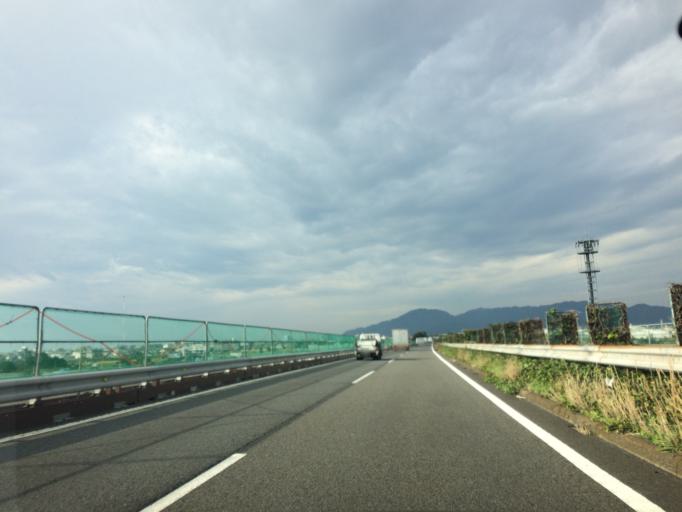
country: JP
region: Shizuoka
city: Shizuoka-shi
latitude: 34.9633
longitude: 138.4248
